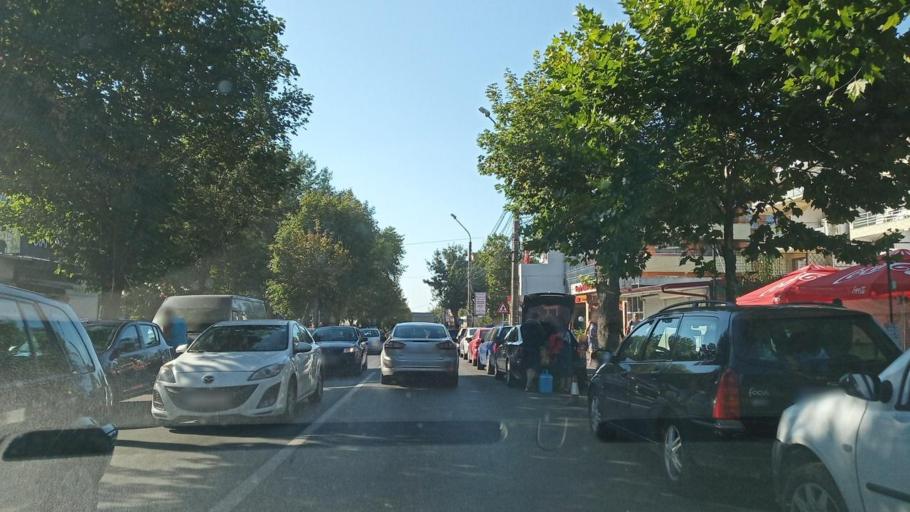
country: RO
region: Constanta
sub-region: Oras Eforie
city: Eforie Nord
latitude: 44.0636
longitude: 28.6346
